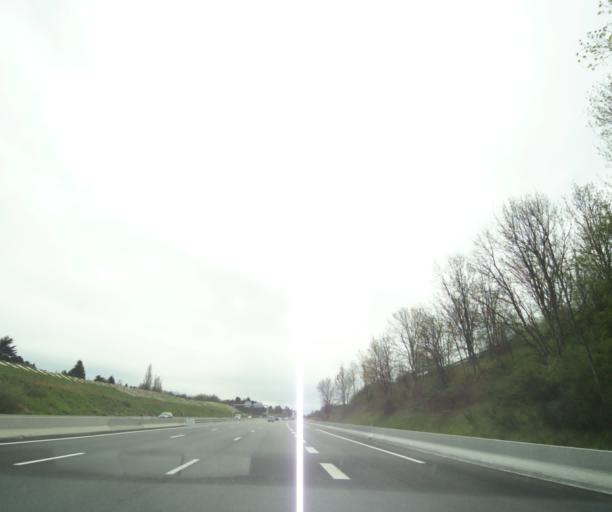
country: FR
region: Rhone-Alpes
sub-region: Departement du Rhone
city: Limonest
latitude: 45.8317
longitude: 4.7603
